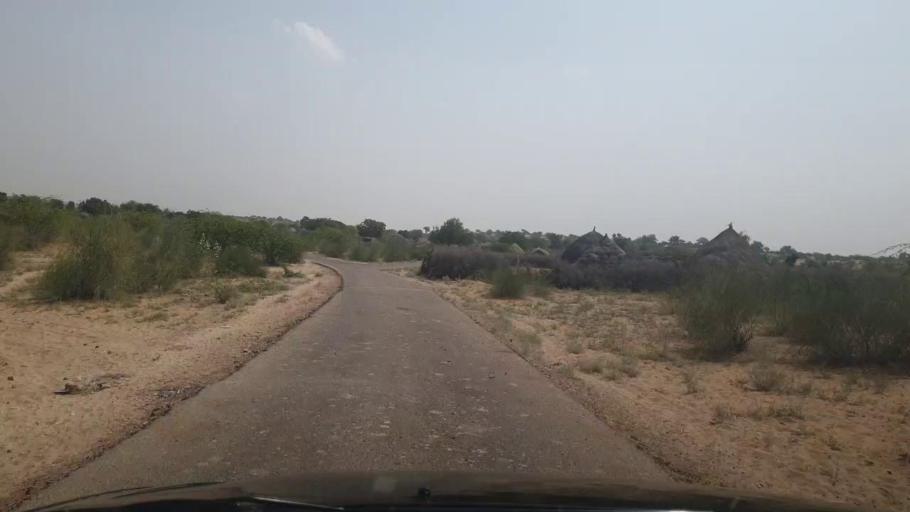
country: PK
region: Sindh
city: Islamkot
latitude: 25.0083
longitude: 70.4082
